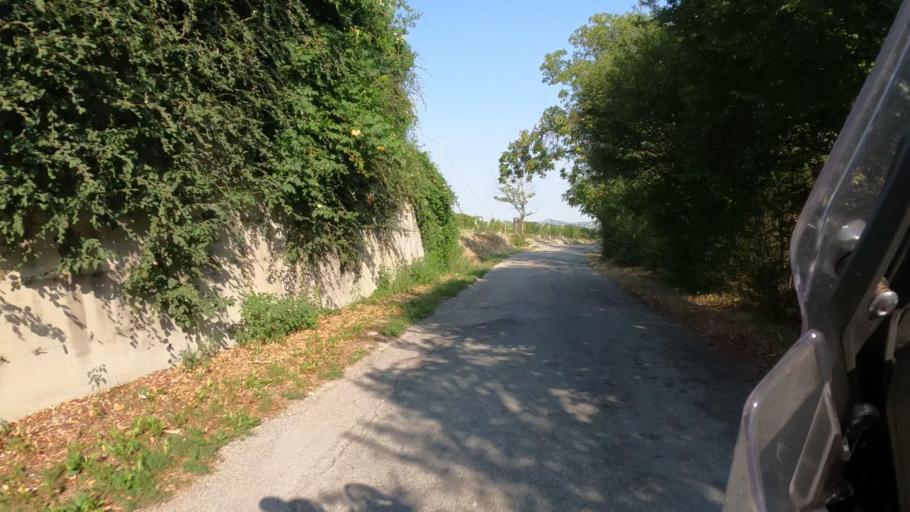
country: IT
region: Piedmont
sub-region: Provincia di Asti
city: Nizza Monferrato
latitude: 44.7587
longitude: 8.3809
